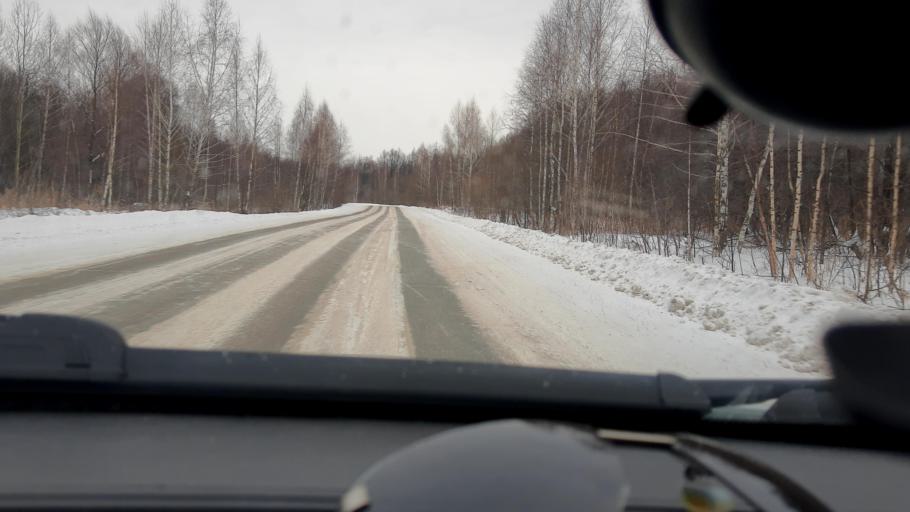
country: RU
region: Bashkortostan
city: Blagoveshchensk
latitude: 55.0327
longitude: 56.0950
